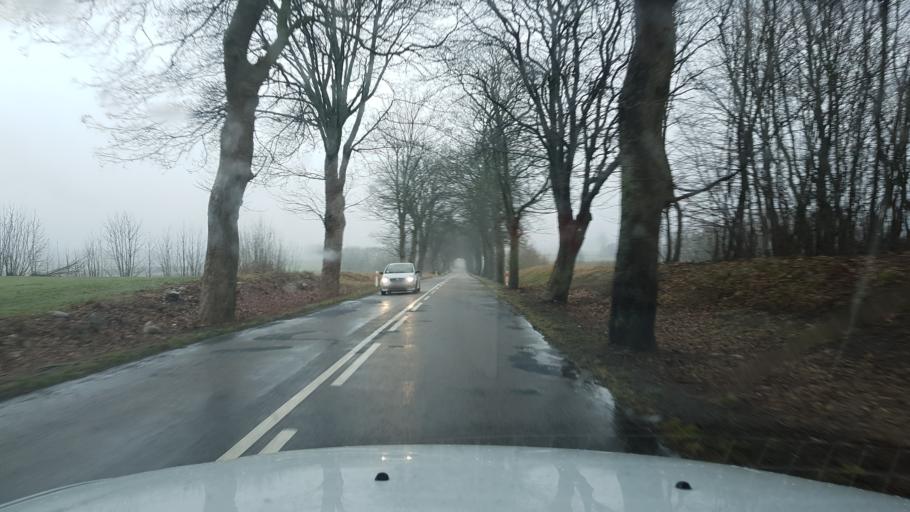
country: PL
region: West Pomeranian Voivodeship
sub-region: Powiat drawski
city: Czaplinek
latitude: 53.5729
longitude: 16.2330
